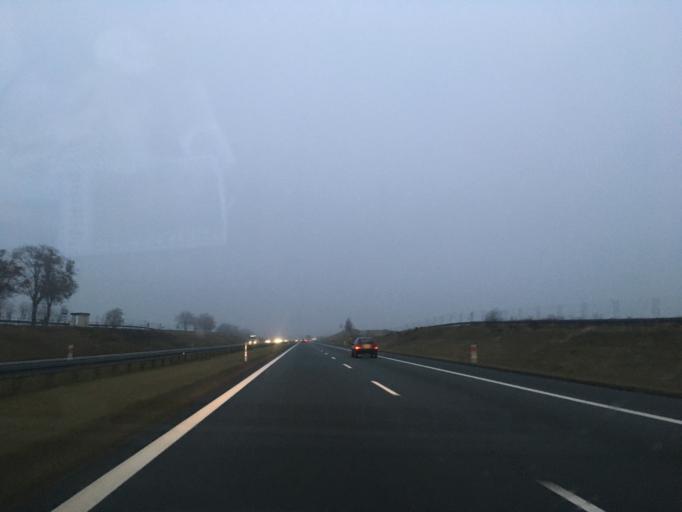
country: PL
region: Warmian-Masurian Voivodeship
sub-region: Powiat ostrodzki
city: Maldyty
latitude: 53.9360
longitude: 19.7037
